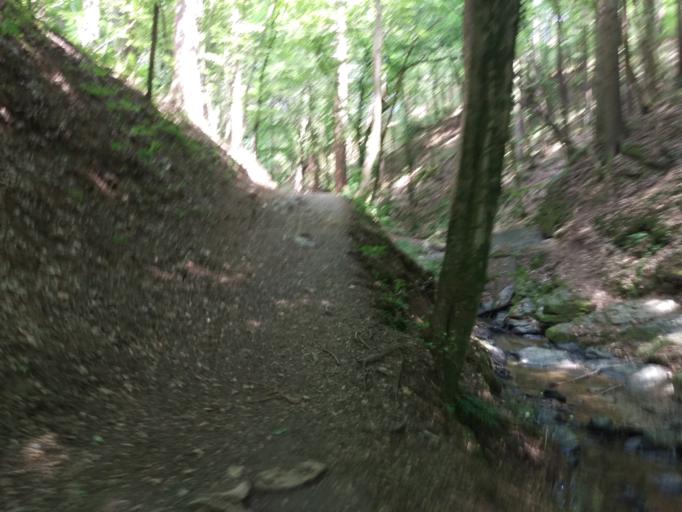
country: AT
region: Styria
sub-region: Graz Stadt
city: Mariatrost
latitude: 47.1094
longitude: 15.4787
